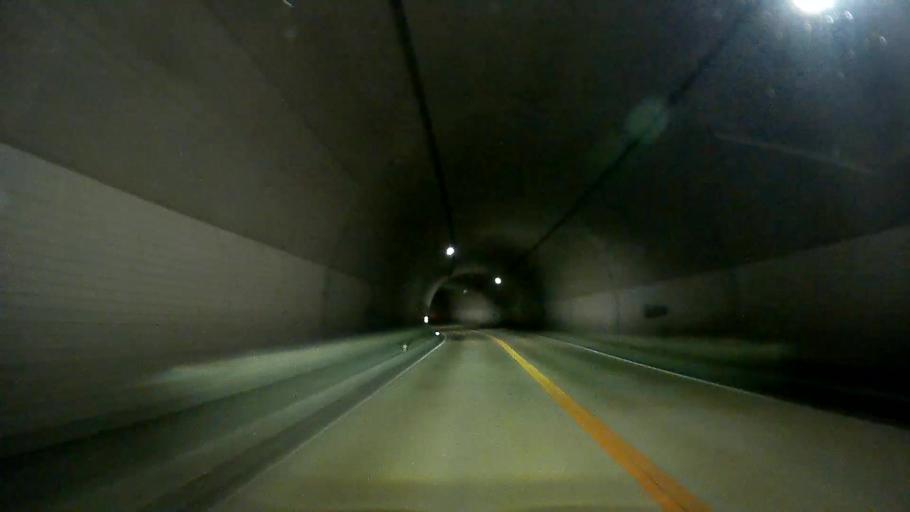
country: JP
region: Saitama
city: Morohongo
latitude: 35.9095
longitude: 139.2371
